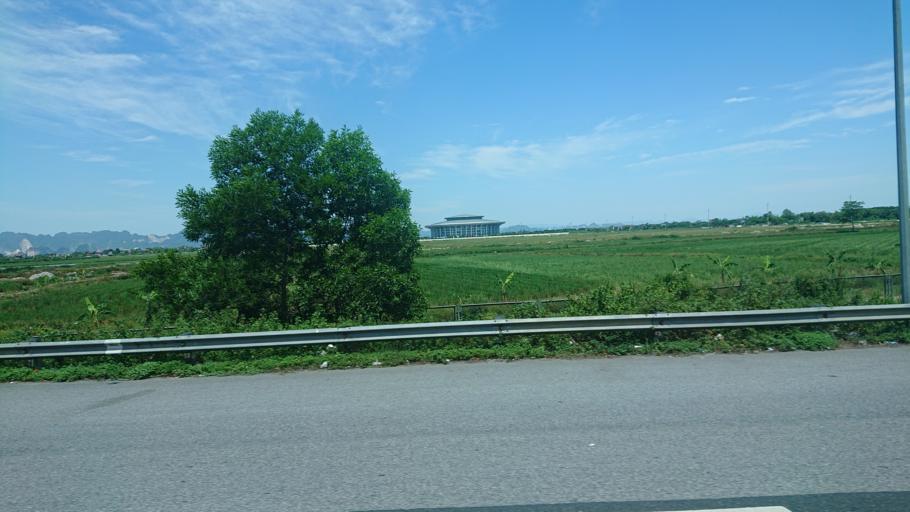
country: VN
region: Ha Nam
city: Thanh Pho Phu Ly
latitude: 20.5693
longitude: 105.9511
